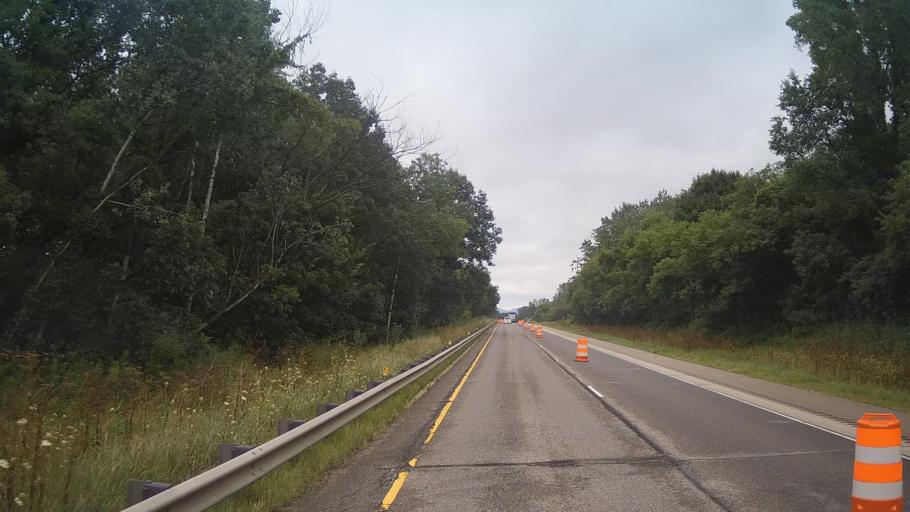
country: US
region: Wisconsin
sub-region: La Crosse County
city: Brice Prairie
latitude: 43.9179
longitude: -91.3741
